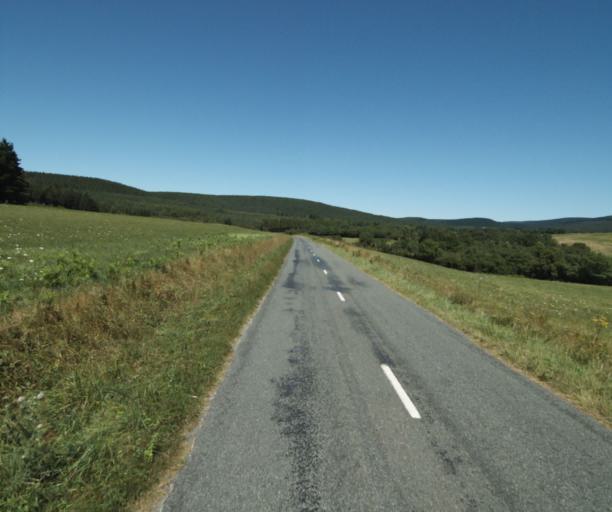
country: FR
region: Midi-Pyrenees
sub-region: Departement du Tarn
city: Dourgne
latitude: 43.4386
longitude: 2.1766
